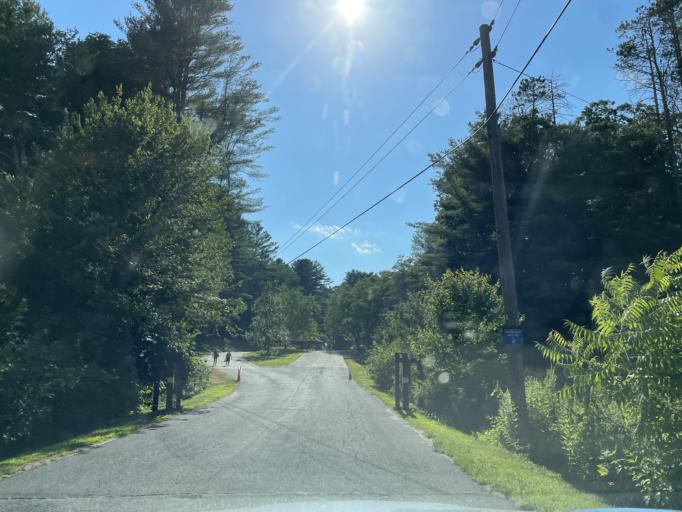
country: US
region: Massachusetts
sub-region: Worcester County
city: Sturbridge
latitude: 42.1468
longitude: -72.0592
